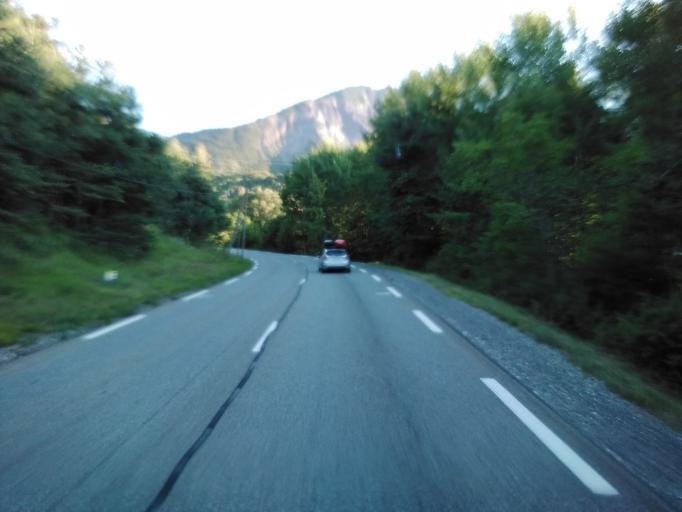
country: FR
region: Provence-Alpes-Cote d'Azur
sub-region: Departement des Hautes-Alpes
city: Chorges
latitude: 44.4622
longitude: 6.2880
